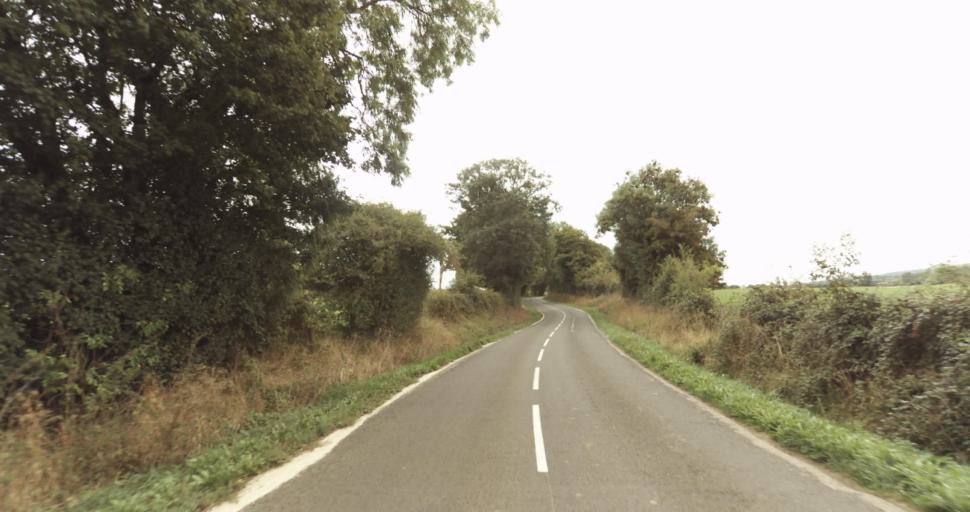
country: FR
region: Lower Normandy
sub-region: Departement de l'Orne
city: Gace
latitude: 48.7160
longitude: 0.3343
